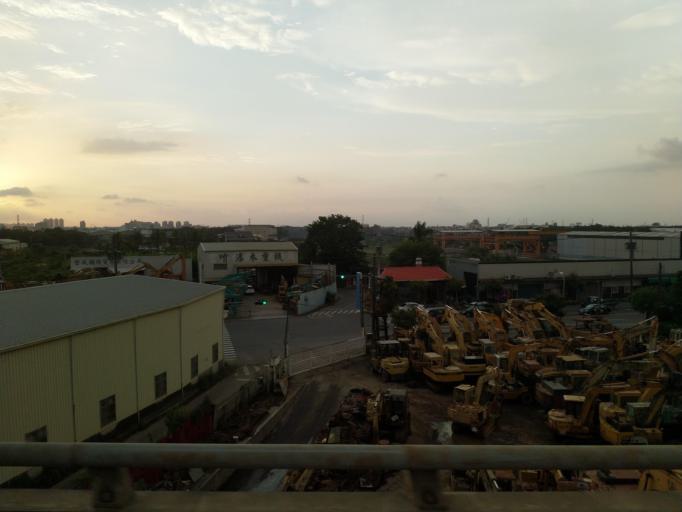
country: TW
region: Taiwan
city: Fengshan
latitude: 22.7483
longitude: 120.3634
